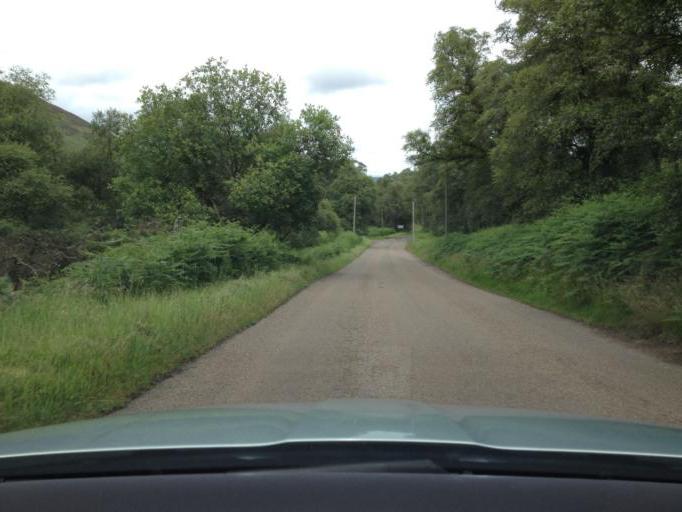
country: GB
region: Scotland
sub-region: Angus
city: Brechin
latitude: 56.8661
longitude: -2.6982
